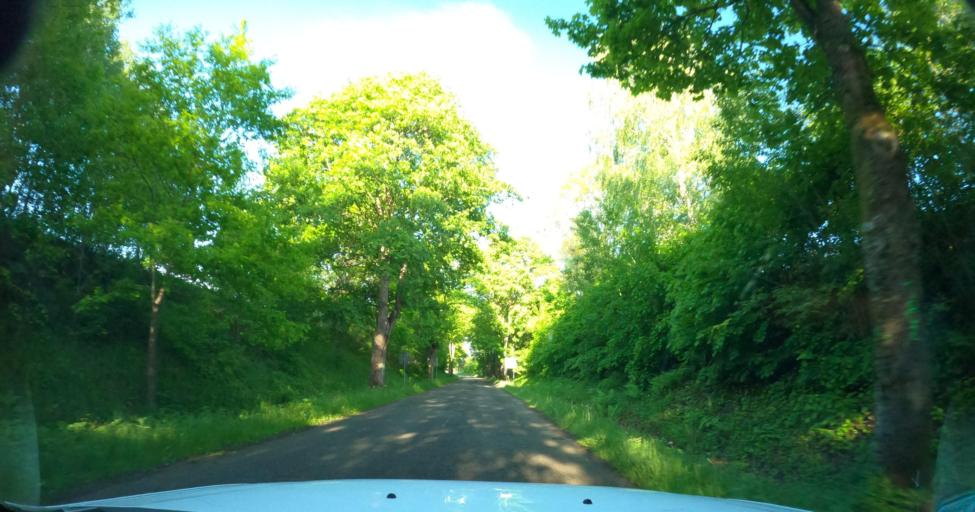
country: PL
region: Warmian-Masurian Voivodeship
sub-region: Powiat braniewski
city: Braniewo
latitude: 54.2811
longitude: 19.8732
